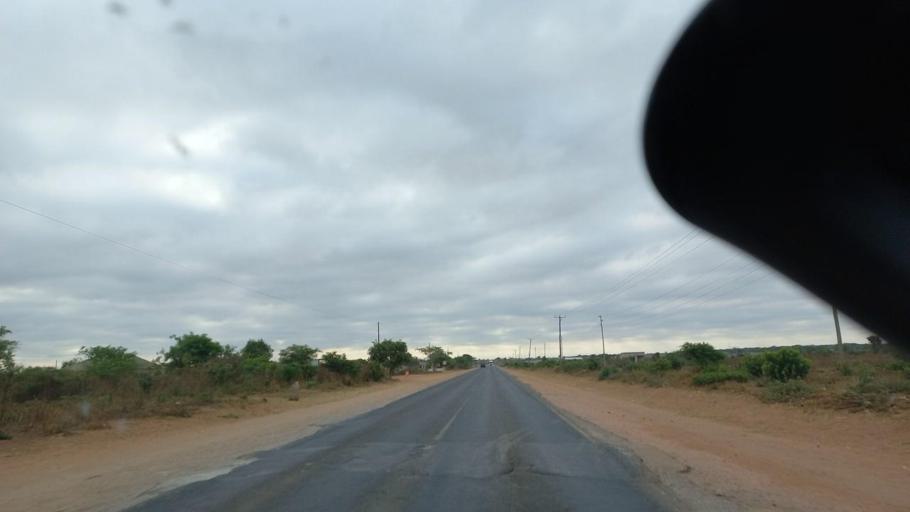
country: ZM
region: Lusaka
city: Chongwe
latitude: -15.3439
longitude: 28.6480
